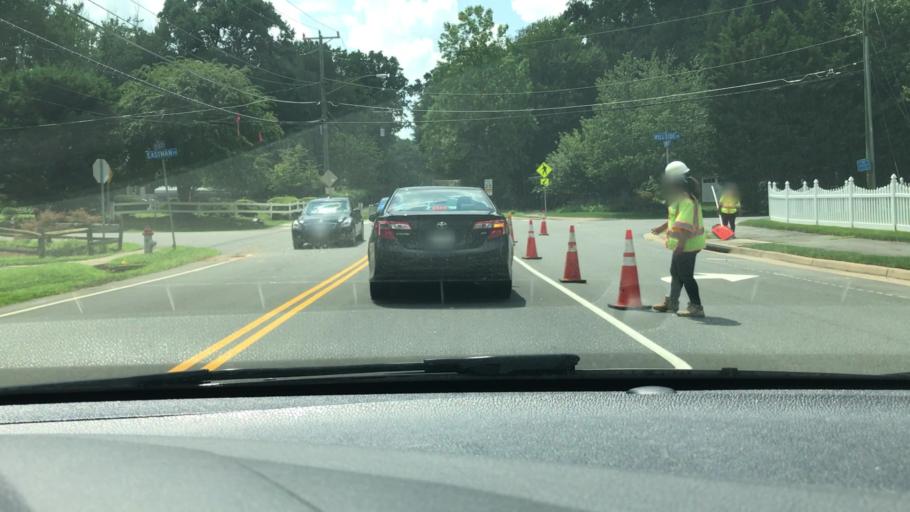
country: US
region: Virginia
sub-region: Fairfax County
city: Pimmit Hills
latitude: 38.9070
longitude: -77.1906
